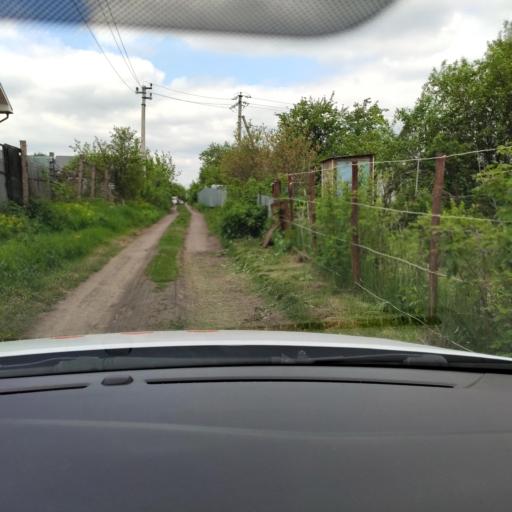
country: RU
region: Tatarstan
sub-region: Gorod Kazan'
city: Kazan
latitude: 55.8692
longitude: 49.1066
